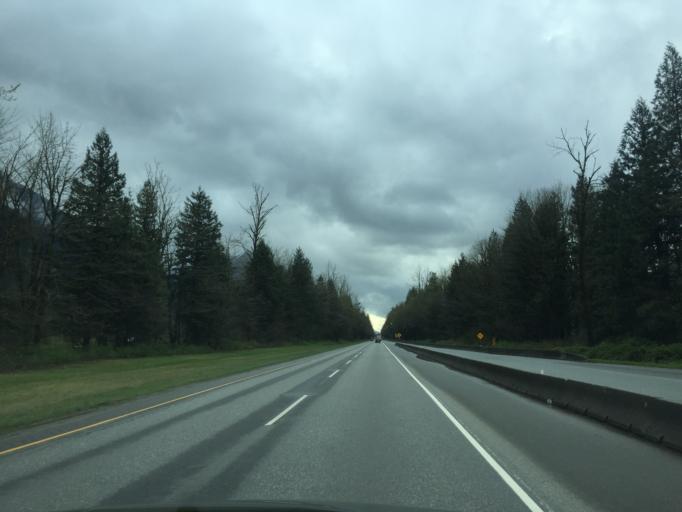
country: CA
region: British Columbia
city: Hope
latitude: 49.3462
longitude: -121.5915
